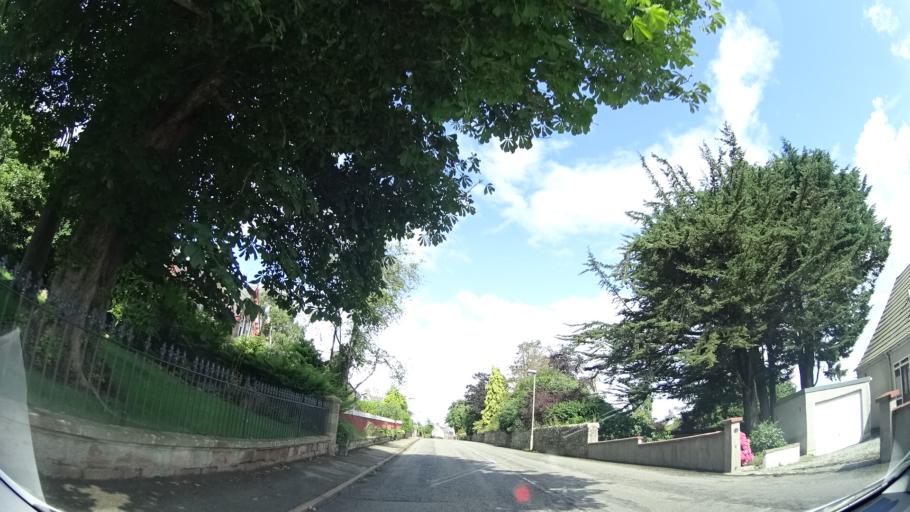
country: GB
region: Scotland
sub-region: Highland
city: Fortrose
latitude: 57.5793
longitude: -4.1358
